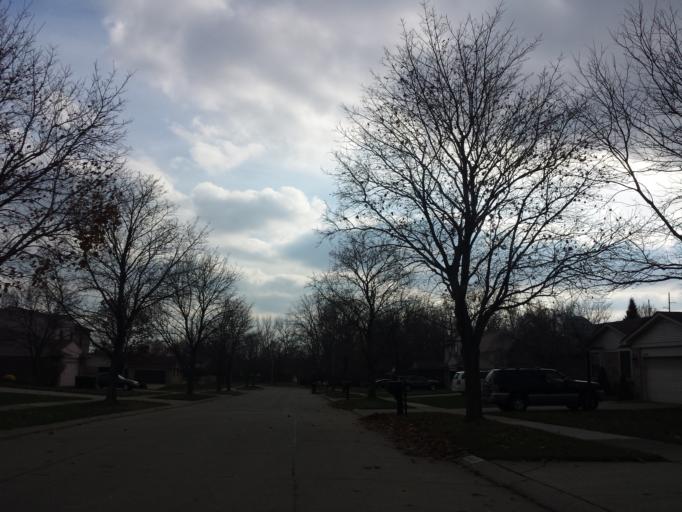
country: US
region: Michigan
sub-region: Wayne County
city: Plymouth
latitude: 42.4073
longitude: -83.4314
